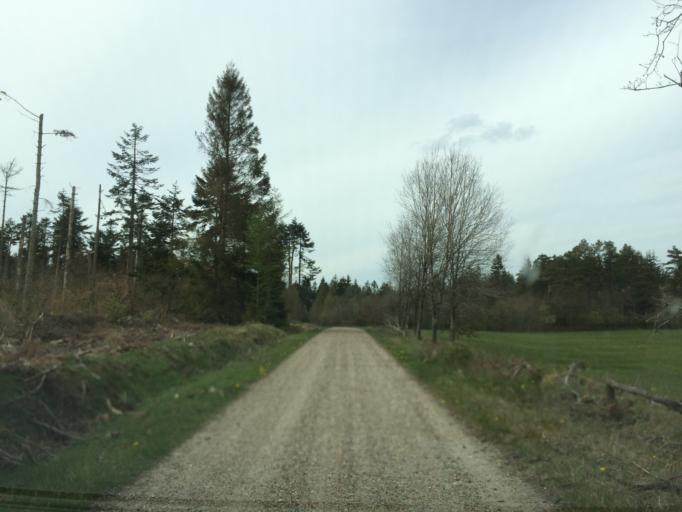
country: DK
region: Central Jutland
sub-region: Holstebro Kommune
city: Ulfborg
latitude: 56.2234
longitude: 8.4697
